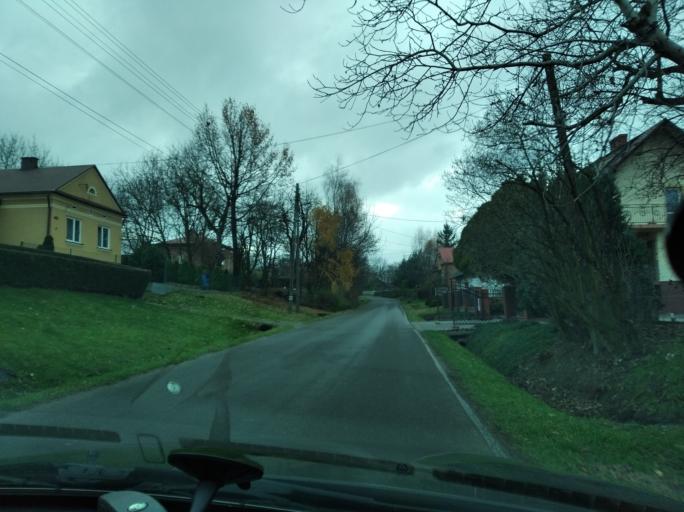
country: PL
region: Subcarpathian Voivodeship
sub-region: Powiat przeworski
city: Sietesz
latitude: 49.9884
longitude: 22.3489
